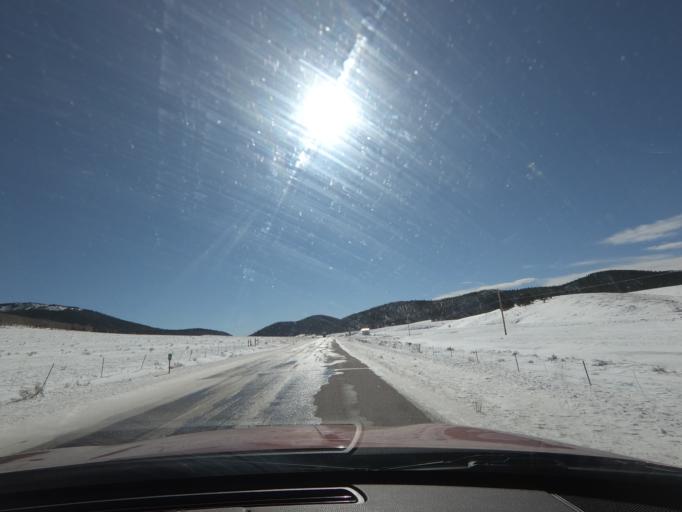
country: US
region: Colorado
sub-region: Teller County
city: Cripple Creek
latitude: 38.7705
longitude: -105.1195
